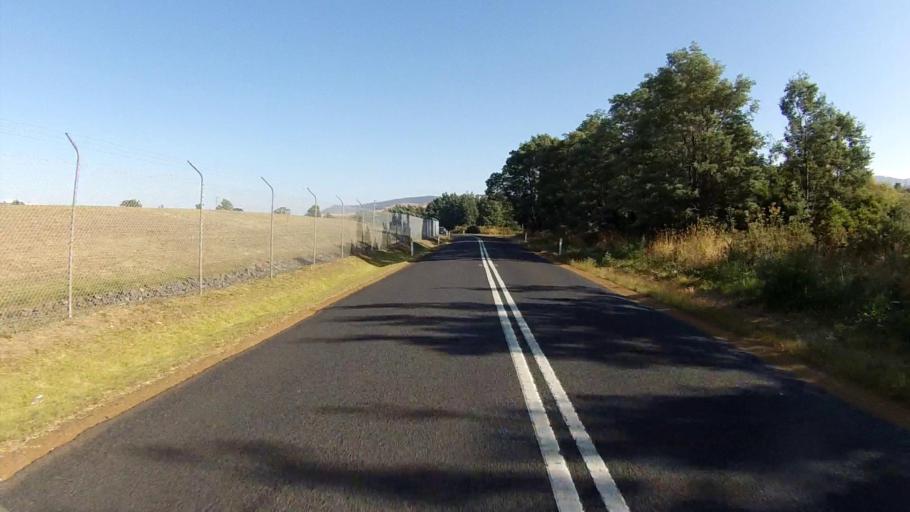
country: AU
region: Tasmania
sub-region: Derwent Valley
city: New Norfolk
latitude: -42.7702
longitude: 147.0263
